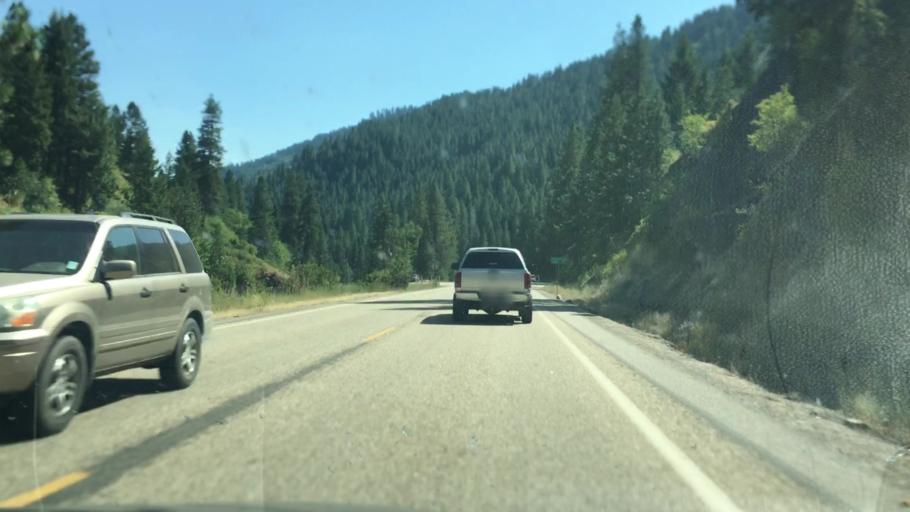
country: US
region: Idaho
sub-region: Valley County
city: Cascade
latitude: 44.1412
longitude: -116.1152
